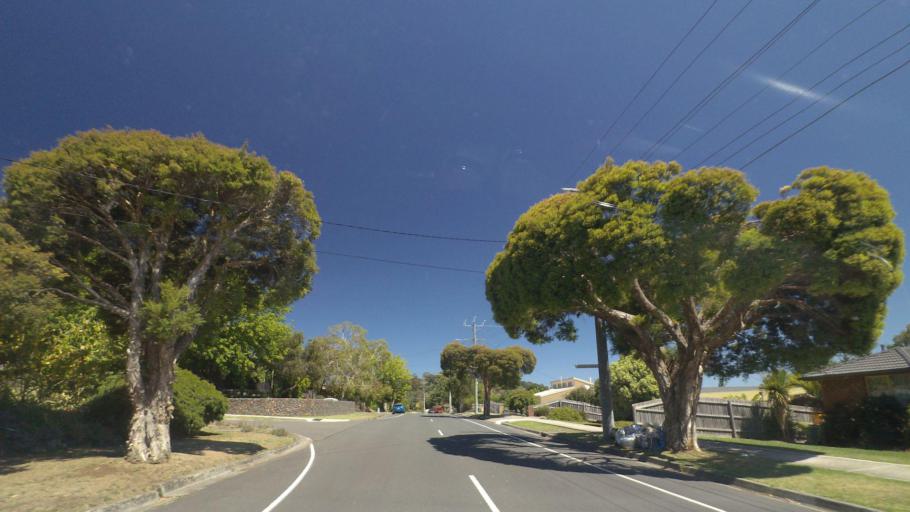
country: AU
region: Victoria
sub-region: Yarra Ranges
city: Chirnside Park
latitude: -37.7545
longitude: 145.3244
